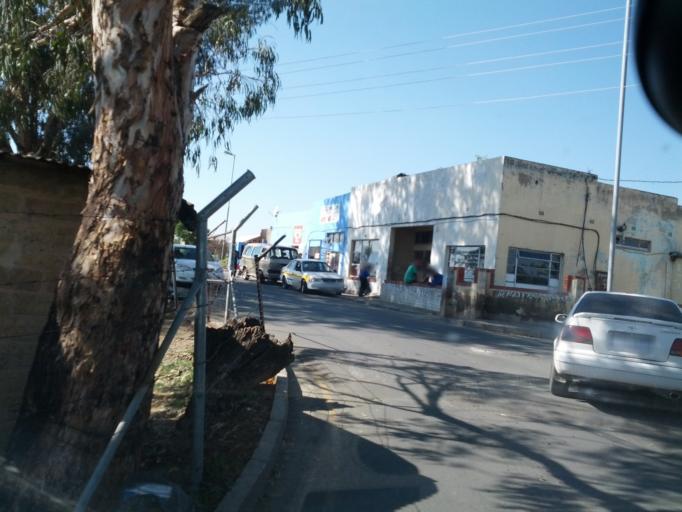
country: LS
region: Maseru
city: Maseru
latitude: -29.3053
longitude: 27.4936
